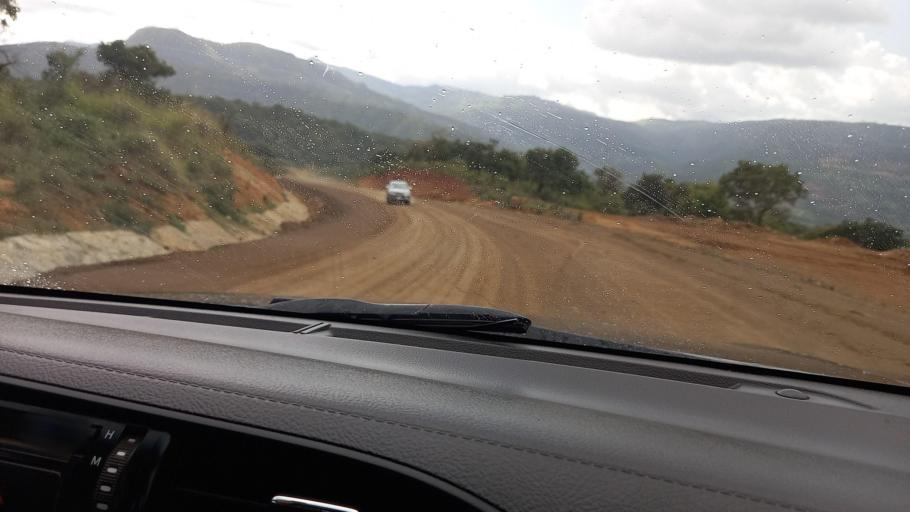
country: ET
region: Southern Nations, Nationalities, and People's Region
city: Mizan Teferi
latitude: 6.1826
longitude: 35.6945
